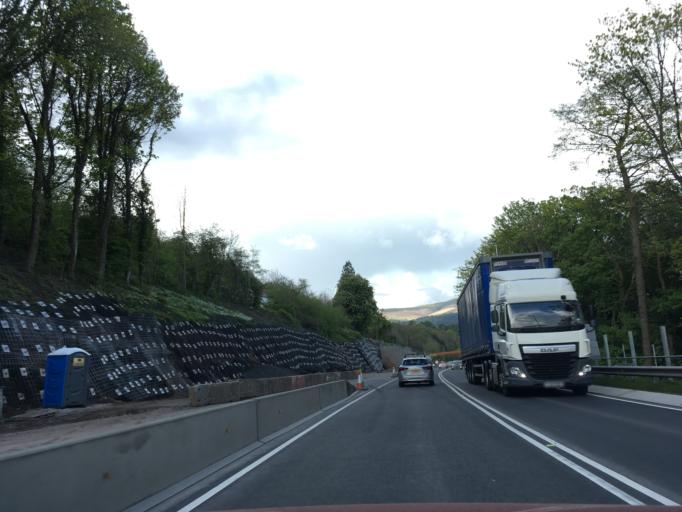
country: GB
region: Wales
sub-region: Monmouthshire
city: Gilwern
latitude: 51.8123
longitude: -3.1215
